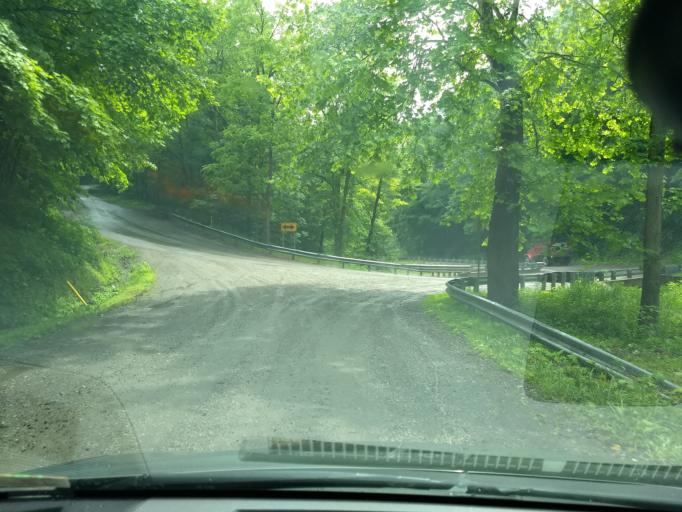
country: US
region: Pennsylvania
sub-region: Armstrong County
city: Orchard Hills
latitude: 40.5682
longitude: -79.5151
